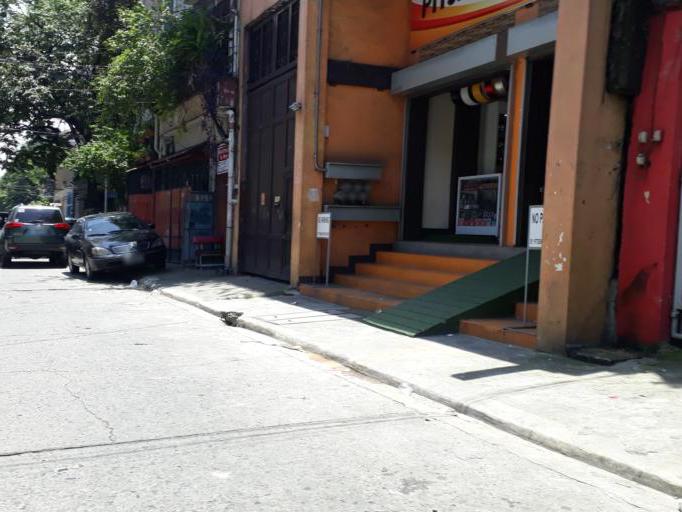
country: PH
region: Calabarzon
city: Del Monte
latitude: 14.6513
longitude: 120.9860
